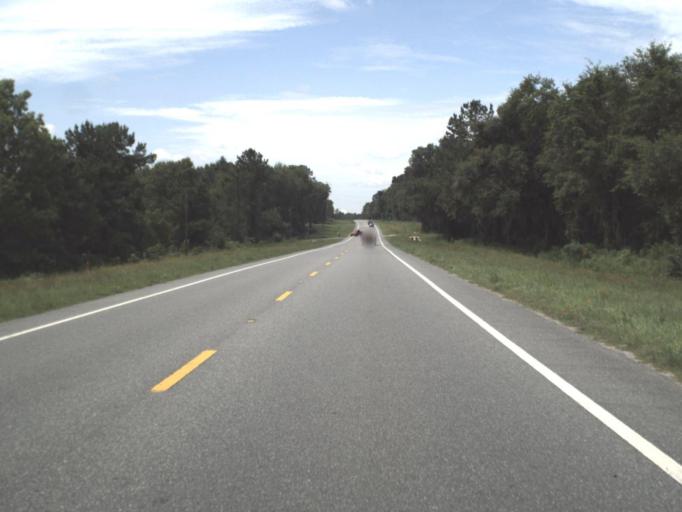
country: US
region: Florida
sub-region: Suwannee County
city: Live Oak
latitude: 30.3737
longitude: -82.9397
